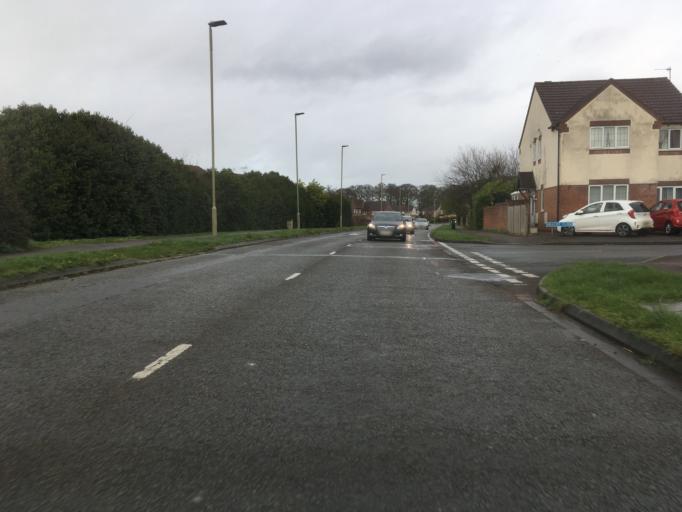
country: GB
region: England
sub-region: Gloucestershire
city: Gloucester
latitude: 51.8277
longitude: -2.2898
